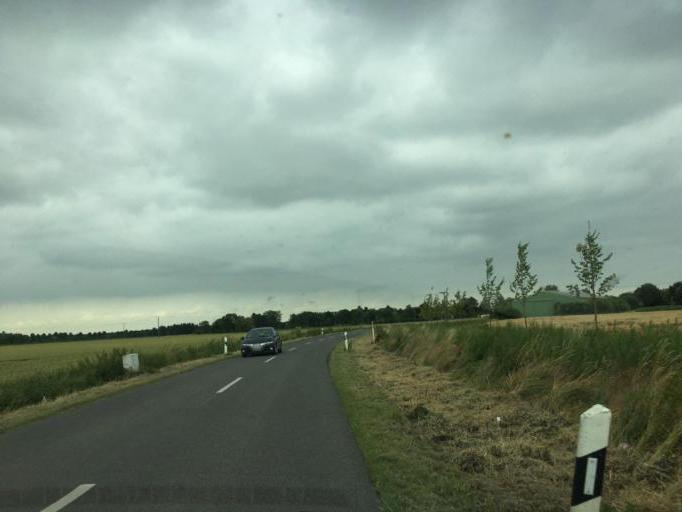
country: DE
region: North Rhine-Westphalia
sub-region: Regierungsbezirk Koln
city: Norvenich
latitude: 50.8129
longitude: 6.6737
